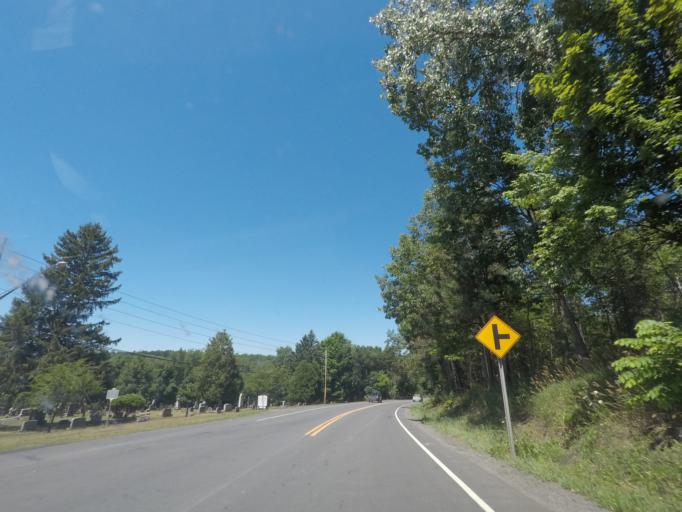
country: US
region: New York
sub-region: Rensselaer County
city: West Sand Lake
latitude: 42.6397
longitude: -73.6054
